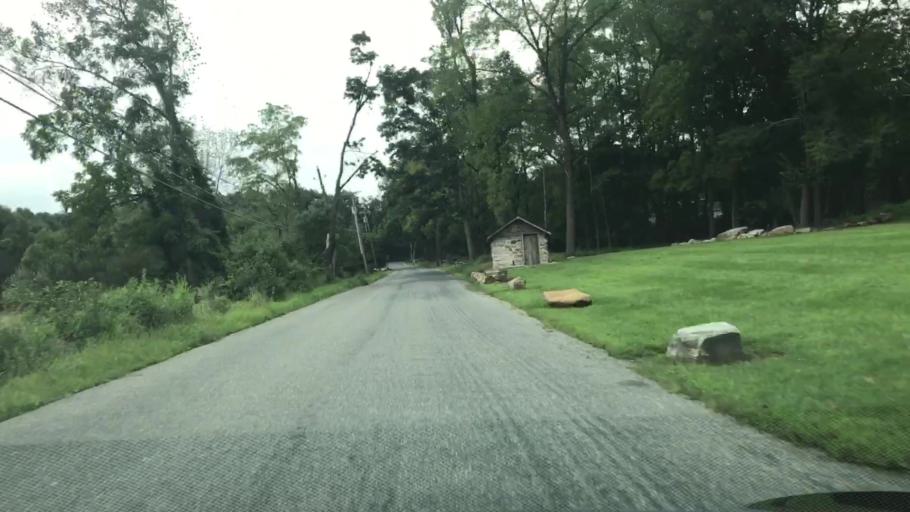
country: US
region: New Jersey
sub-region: Hunterdon County
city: Lebanon
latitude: 40.6702
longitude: -74.8437
